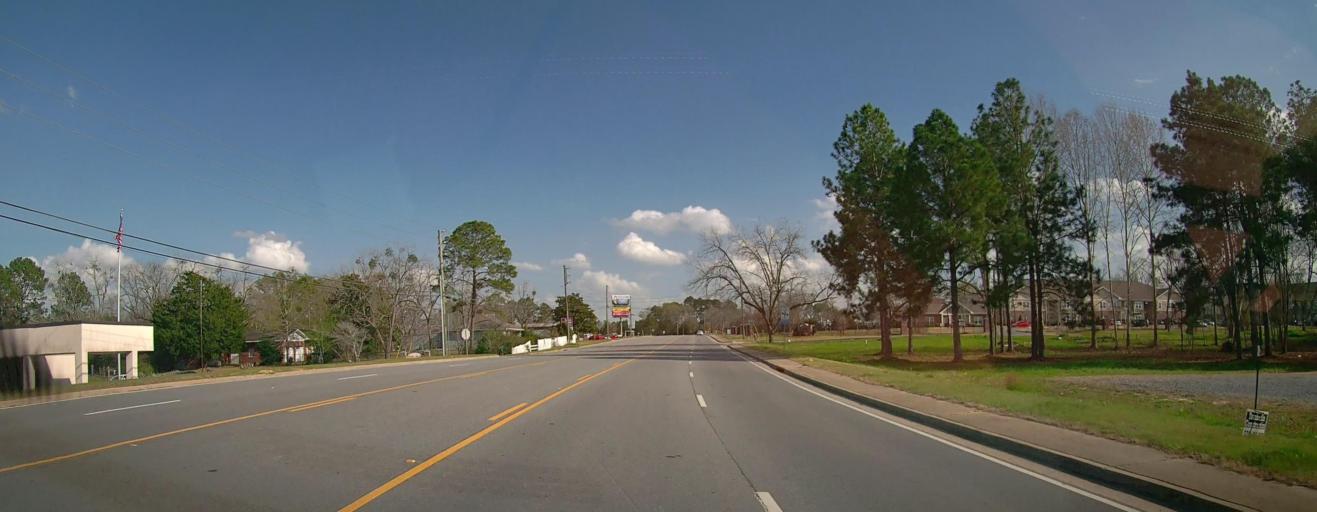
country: US
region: Georgia
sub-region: Telfair County
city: McRae
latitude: 32.0625
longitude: -82.8839
